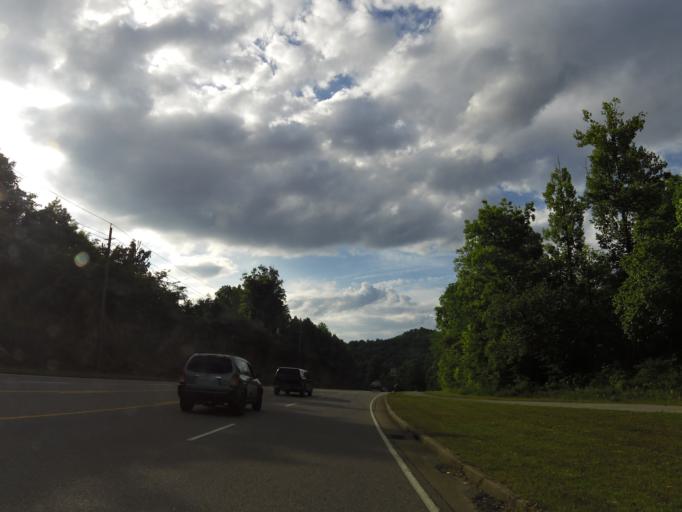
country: US
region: Tennessee
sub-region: Blount County
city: Wildwood
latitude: 35.6760
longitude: -83.7667
